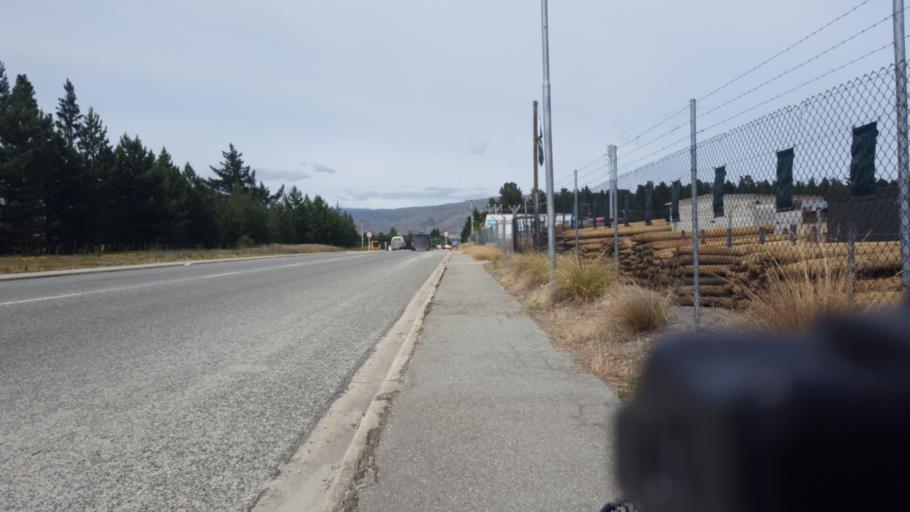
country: NZ
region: Otago
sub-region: Queenstown-Lakes District
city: Wanaka
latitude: -45.0540
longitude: 169.1943
